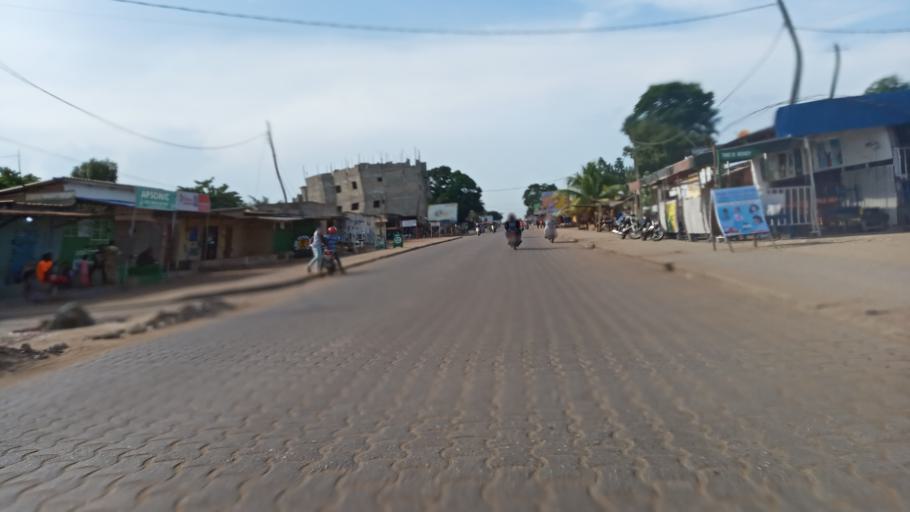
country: TG
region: Maritime
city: Lome
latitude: 6.1586
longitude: 1.2660
